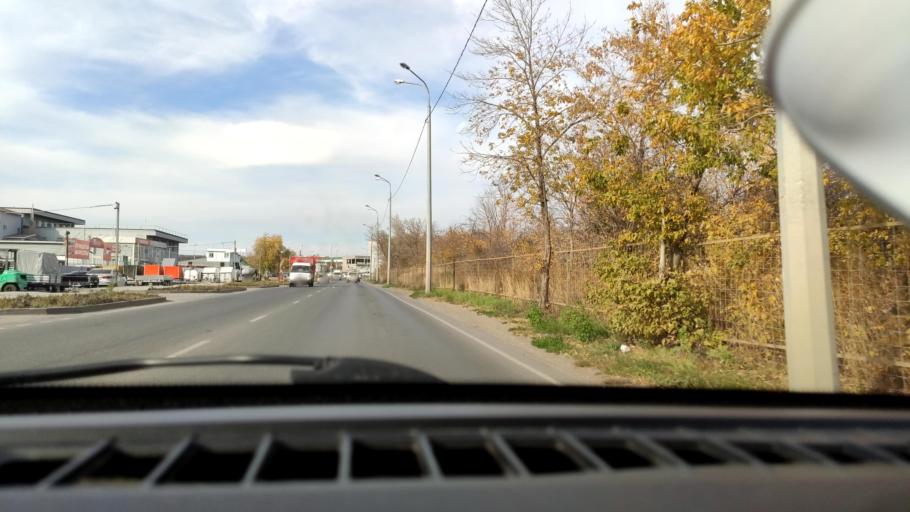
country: RU
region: Samara
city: Petra-Dubrava
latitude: 53.2683
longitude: 50.2594
